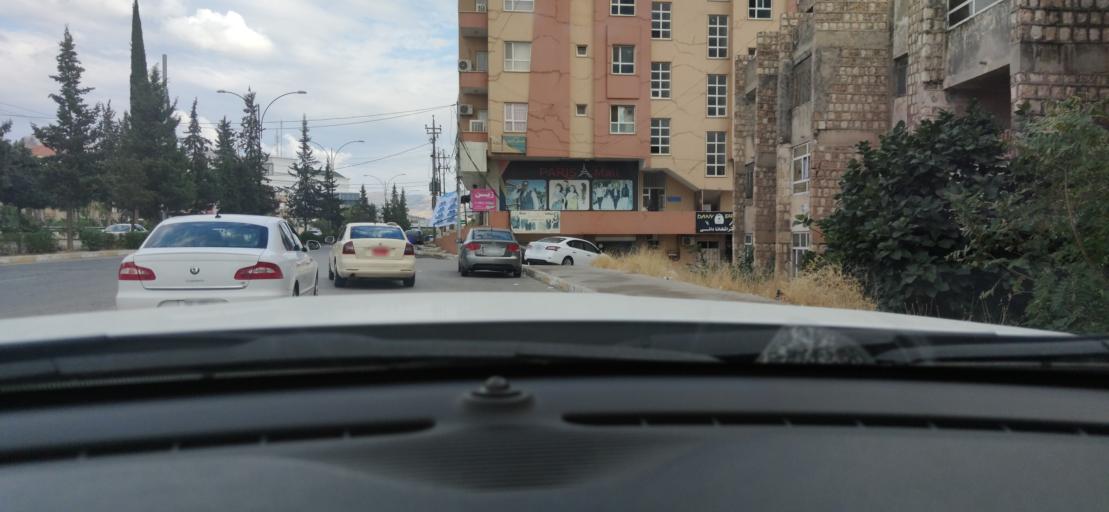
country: IQ
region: Dahuk
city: Dihok
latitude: 36.8669
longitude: 42.9807
